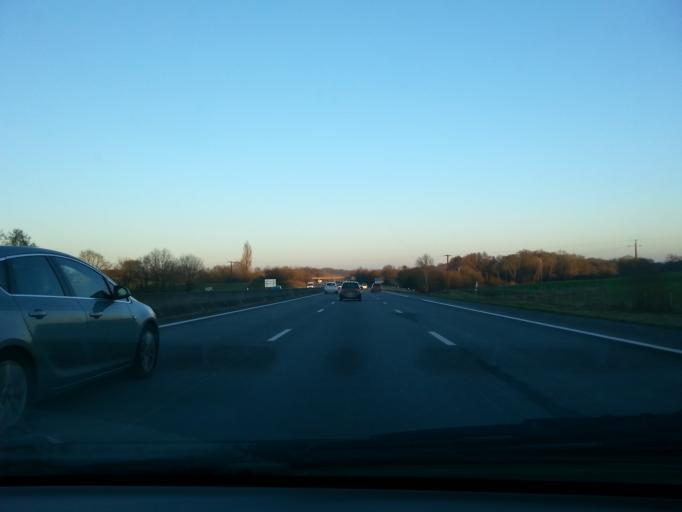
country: FR
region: Centre
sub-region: Departement d'Eure-et-Loir
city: Authon-du-Perche
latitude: 48.2178
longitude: 0.9557
